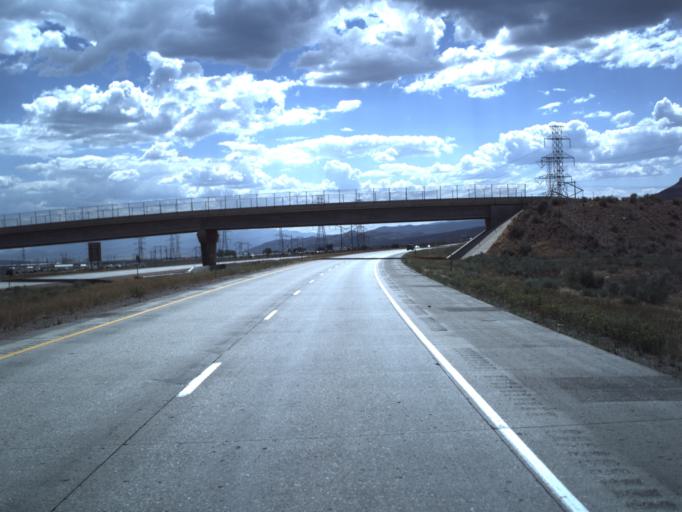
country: US
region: Utah
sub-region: Sevier County
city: Aurora
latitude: 38.8613
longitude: -111.9835
